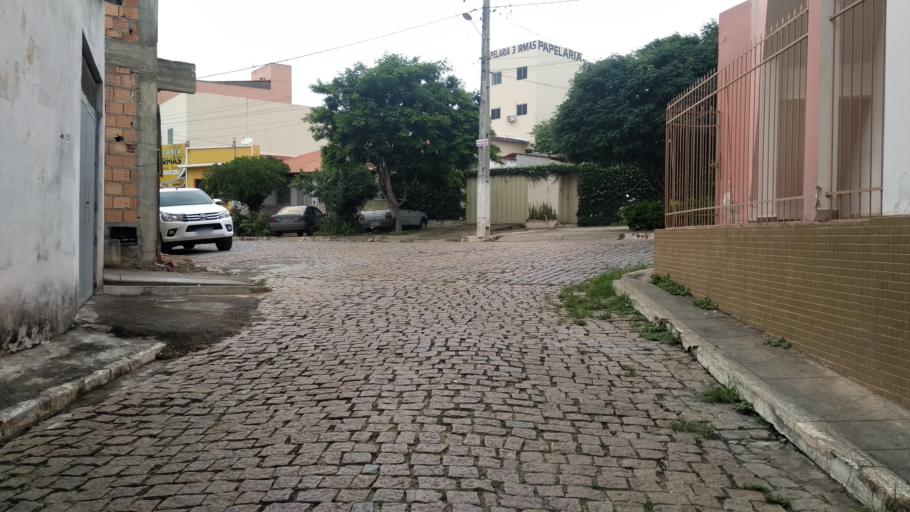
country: BR
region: Bahia
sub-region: Caetite
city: Caetite
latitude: -14.0700
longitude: -42.4859
